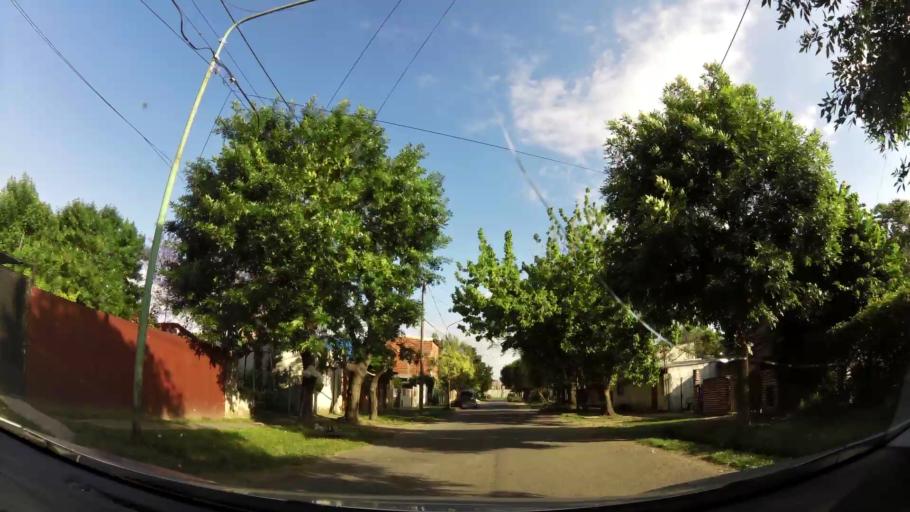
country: AR
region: Buenos Aires
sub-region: Partido de Tigre
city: Tigre
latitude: -34.4690
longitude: -58.6644
